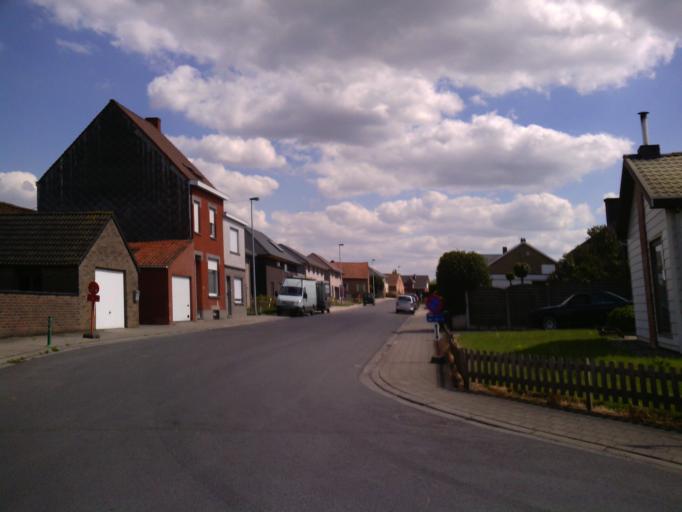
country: BE
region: Flanders
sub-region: Provincie West-Vlaanderen
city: Wevelgem
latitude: 50.7936
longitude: 3.1696
